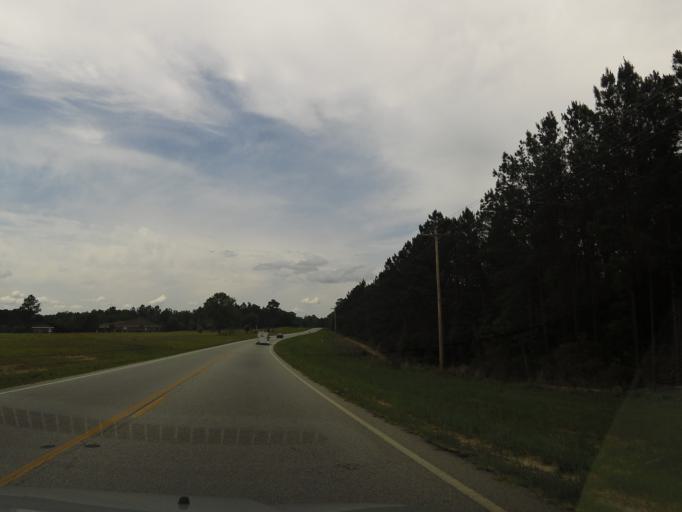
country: US
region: Georgia
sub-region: Emanuel County
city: Swainsboro
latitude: 32.5051
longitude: -82.2593
